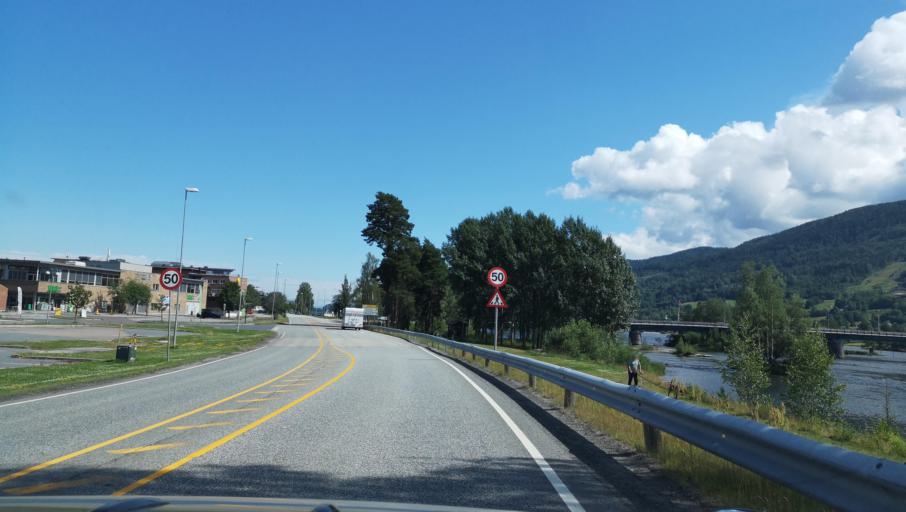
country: NO
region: Buskerud
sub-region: Modum
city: Vikersund
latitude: 59.9639
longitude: 9.9935
